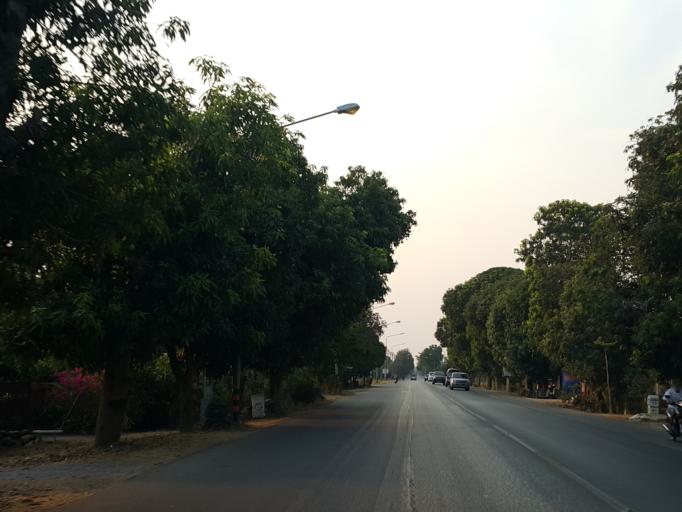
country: TH
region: Sukhothai
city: Si Samrong
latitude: 17.2122
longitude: 99.8661
